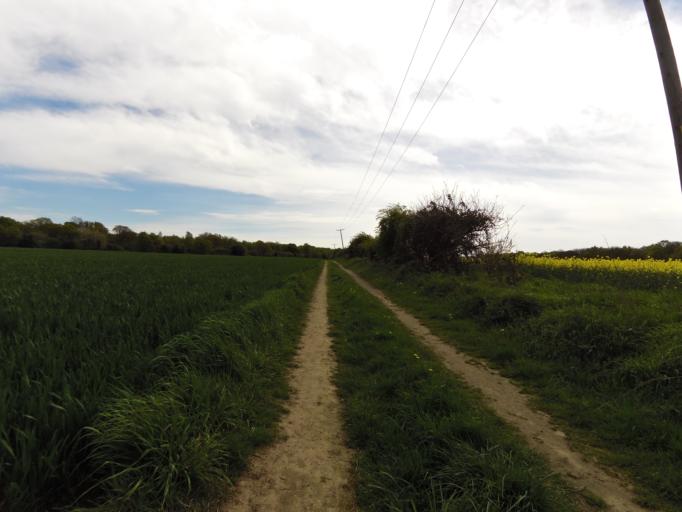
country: GB
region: England
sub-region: Suffolk
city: Ipswich
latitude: 52.0095
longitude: 1.1375
